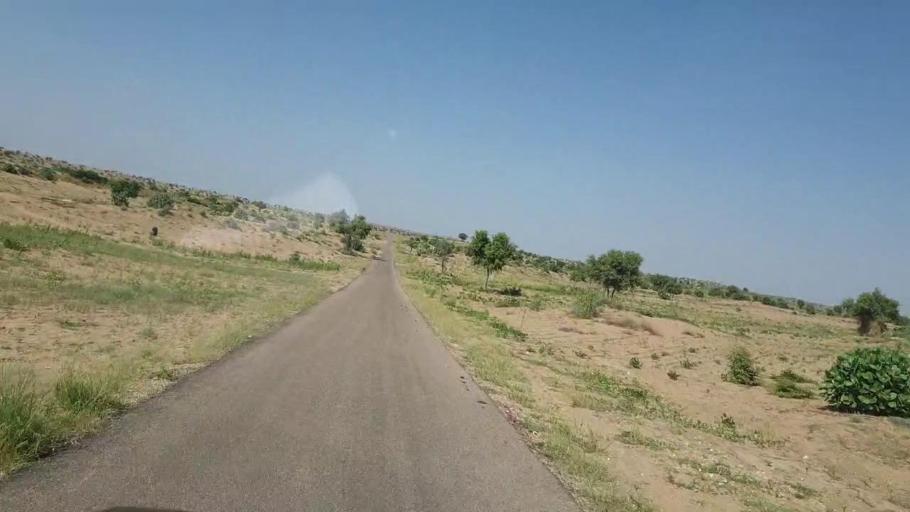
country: PK
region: Sindh
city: Chor
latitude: 25.6289
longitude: 70.3172
